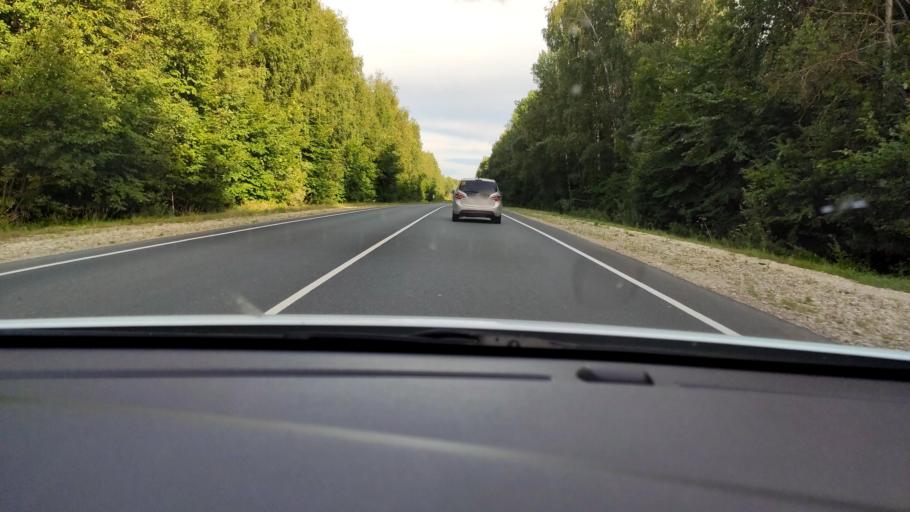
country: RU
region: Mariy-El
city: Krasnogorskiy
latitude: 56.1843
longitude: 48.2564
